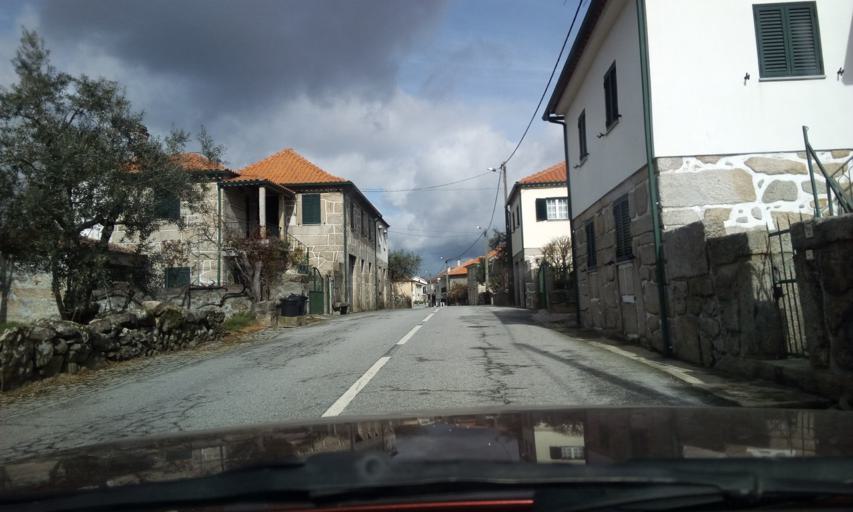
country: PT
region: Guarda
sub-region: Fornos de Algodres
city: Fornos de Algodres
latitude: 40.6494
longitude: -7.5470
